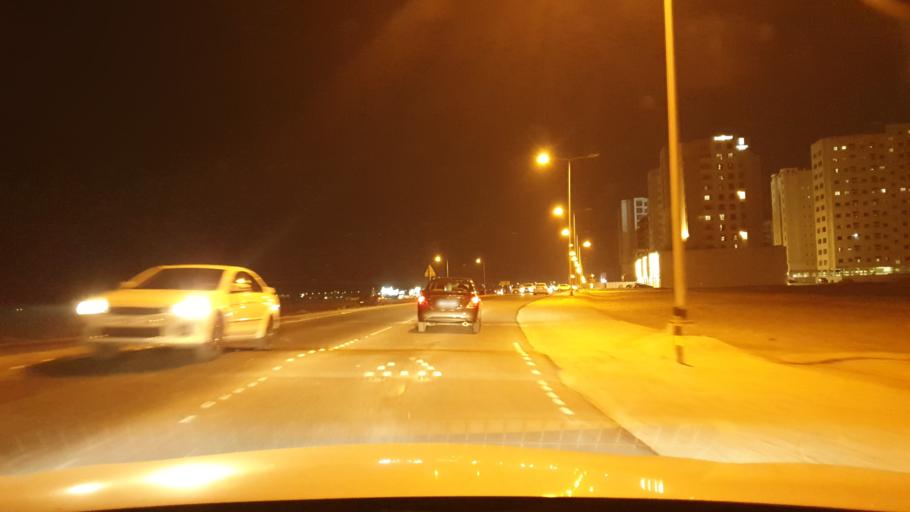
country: BH
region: Muharraq
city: Al Muharraq
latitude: 26.2614
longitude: 50.5945
